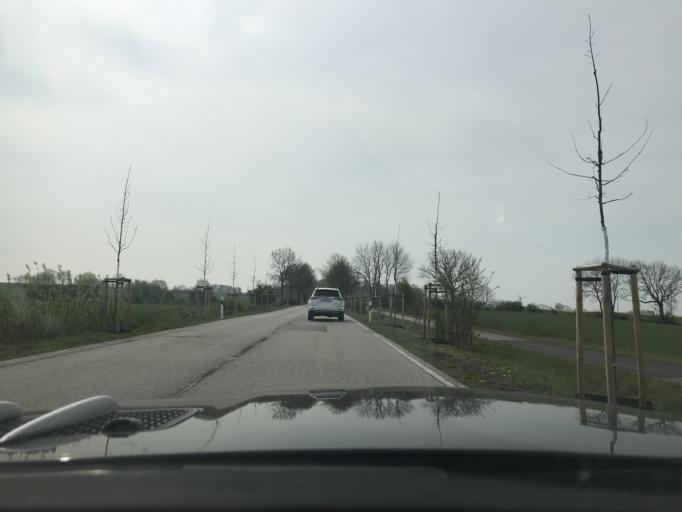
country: DE
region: Schleswig-Holstein
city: Heringsdorf
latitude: 54.2953
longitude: 11.0134
